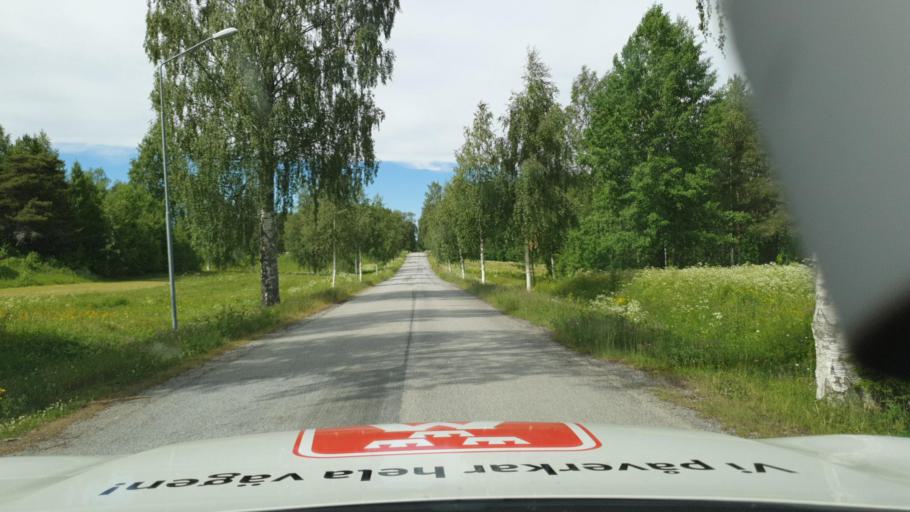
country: SE
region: Vaesterbotten
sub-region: Skelleftea Kommun
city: Burtraesk
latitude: 64.4215
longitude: 20.5411
